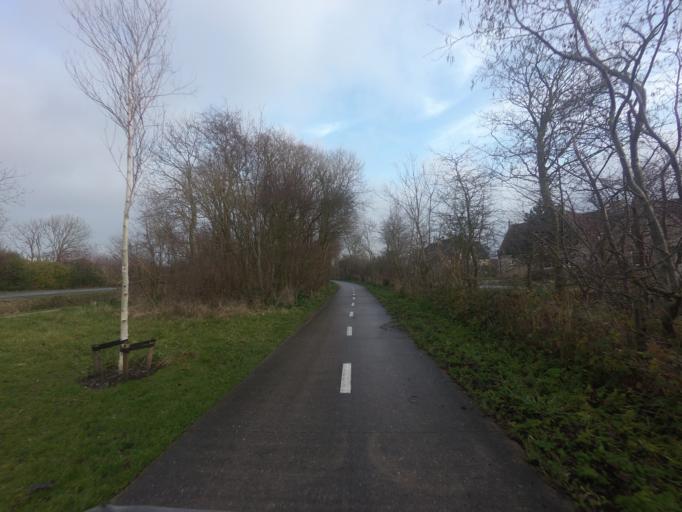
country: NL
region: North Holland
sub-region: Gemeente Texel
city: Den Burg
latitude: 53.1560
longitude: 4.8517
